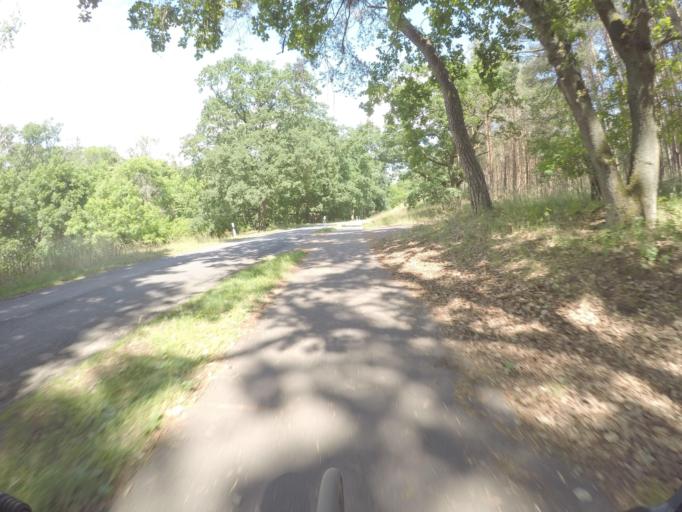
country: DE
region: Brandenburg
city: Roskow
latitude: 52.4419
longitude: 12.7219
